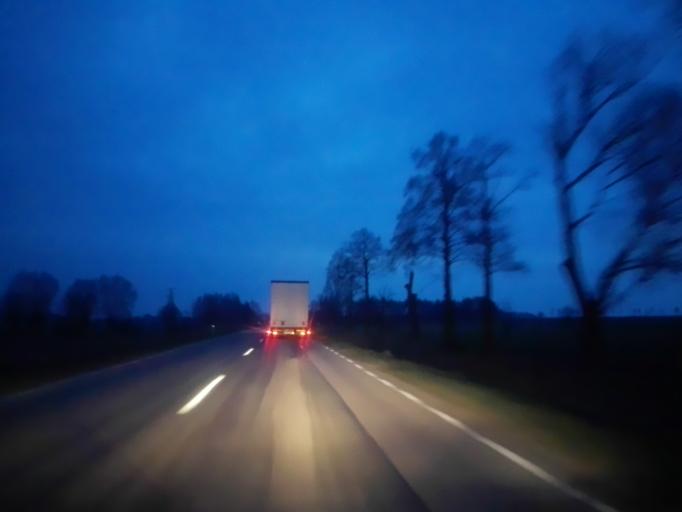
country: PL
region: Podlasie
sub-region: Powiat lomzynski
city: Sniadowo
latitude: 53.0566
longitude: 21.9985
